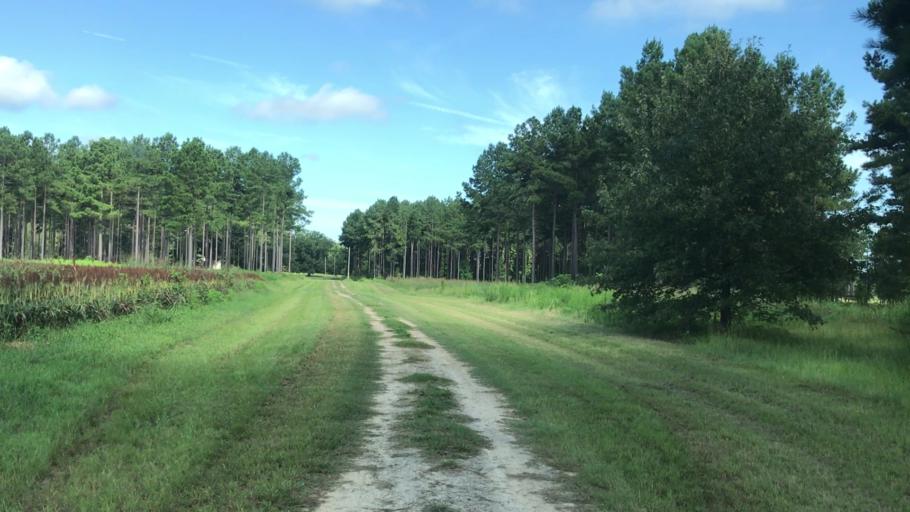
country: US
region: Georgia
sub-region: Jefferson County
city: Wadley
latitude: 32.8157
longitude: -82.3291
